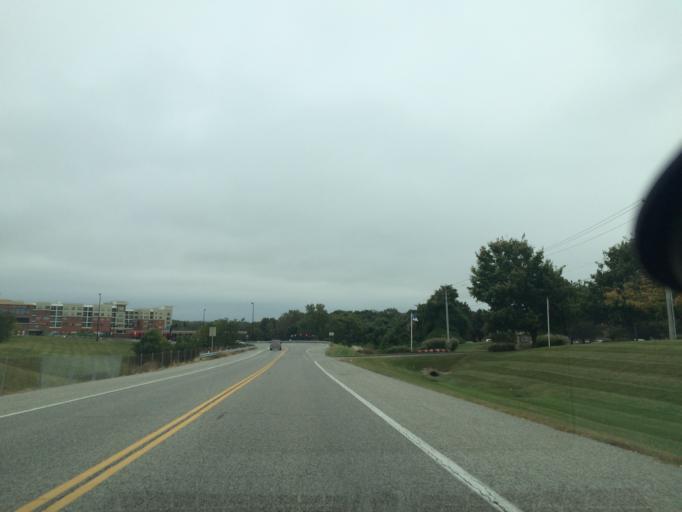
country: US
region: Missouri
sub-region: Saint Charles County
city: Saint Charles
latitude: 38.7680
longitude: -90.4973
